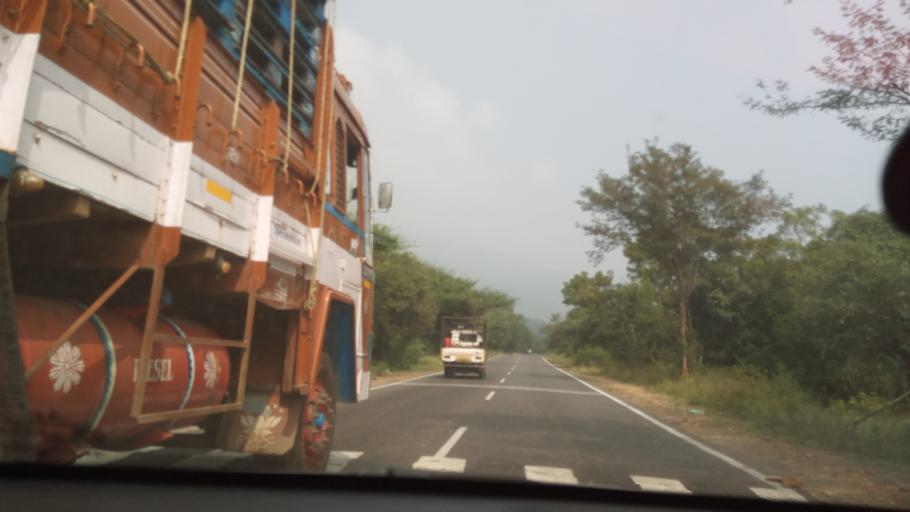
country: IN
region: Tamil Nadu
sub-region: Erode
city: Sathyamangalam
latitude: 11.5751
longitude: 77.1335
